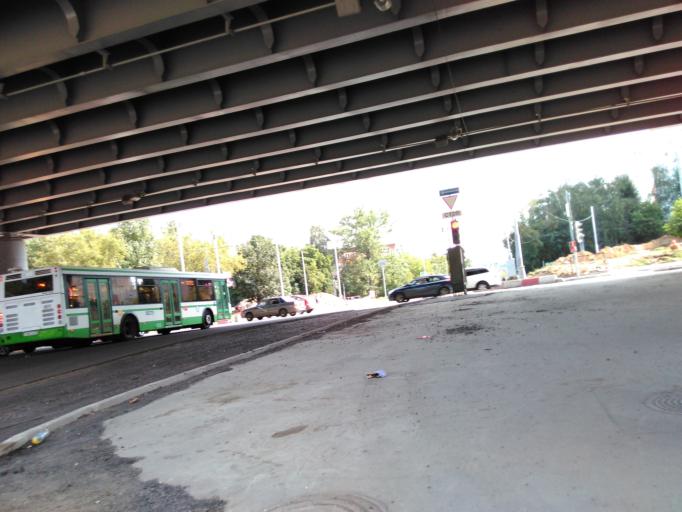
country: RU
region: Moskovskaya
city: Bol'shaya Setun'
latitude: 55.7161
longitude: 37.4019
